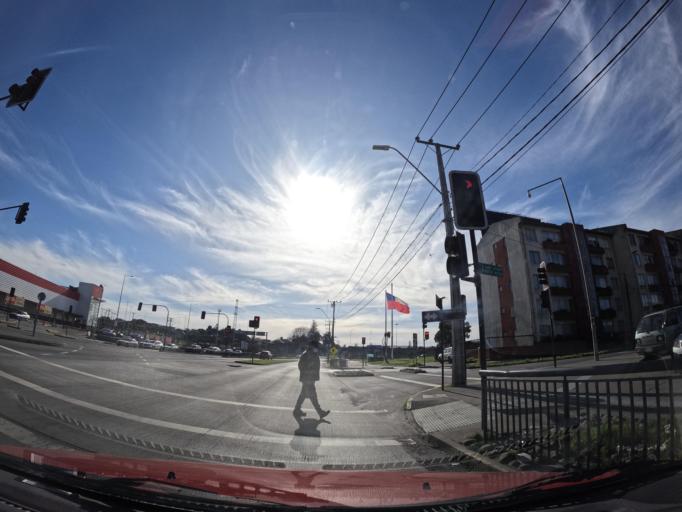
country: CL
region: Biobio
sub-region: Provincia de Concepcion
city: Concepcion
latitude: -36.8079
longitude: -73.0779
